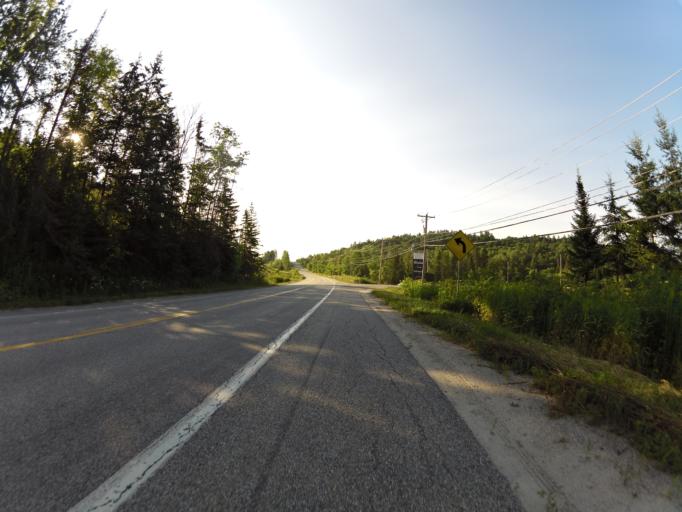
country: CA
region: Quebec
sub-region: Outaouais
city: Wakefield
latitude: 45.6120
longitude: -75.9129
